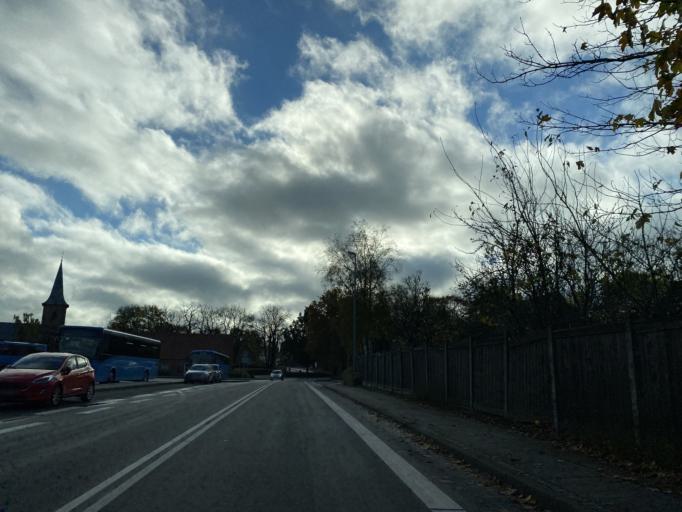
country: DK
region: Central Jutland
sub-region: Favrskov Kommune
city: Hammel
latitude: 56.2569
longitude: 9.8622
